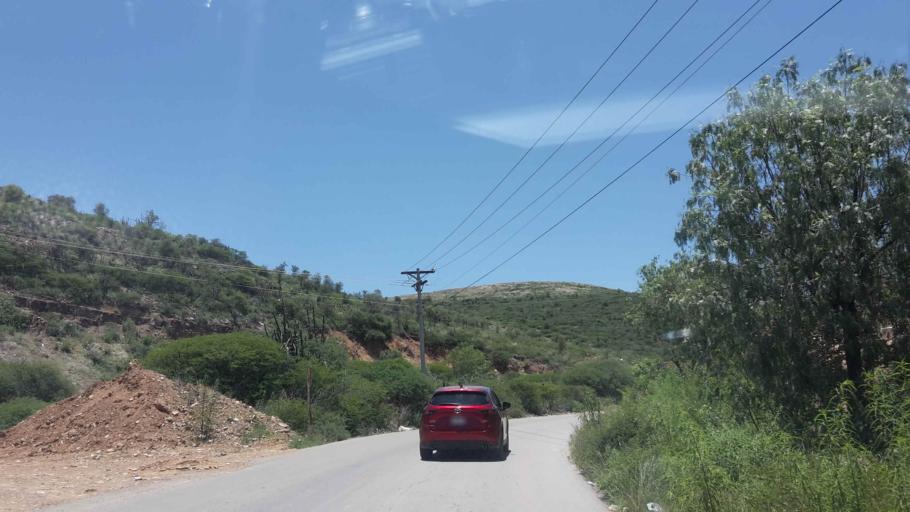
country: BO
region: Cochabamba
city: Tarata
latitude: -17.5241
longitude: -66.0880
